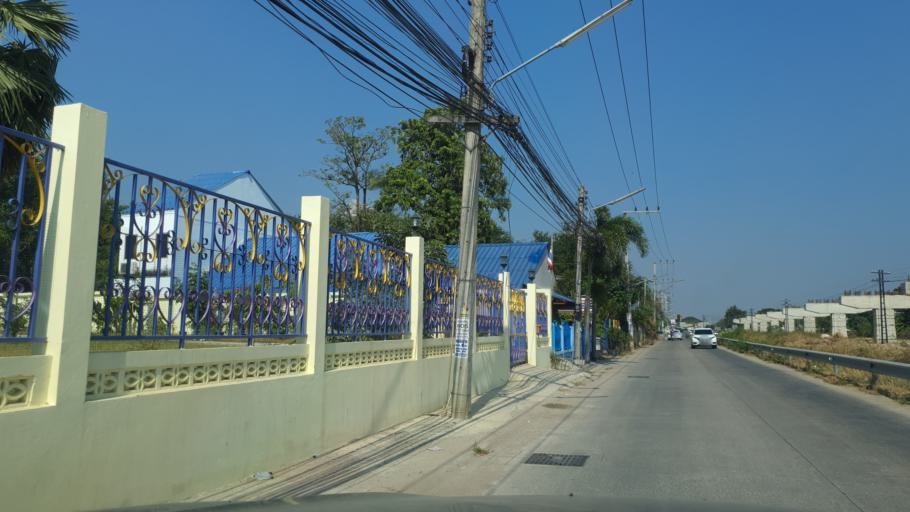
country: TH
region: Prachuap Khiri Khan
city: Hua Hin
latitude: 12.5583
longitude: 99.9566
